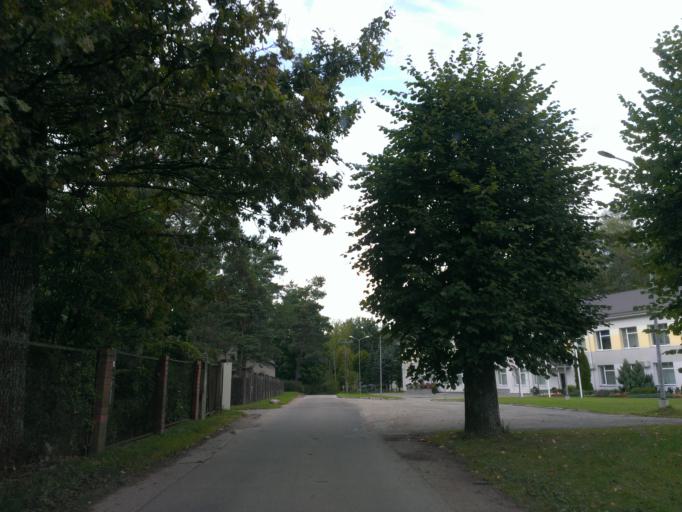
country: LV
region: Ikskile
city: Ikskile
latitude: 56.8359
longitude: 24.4919
